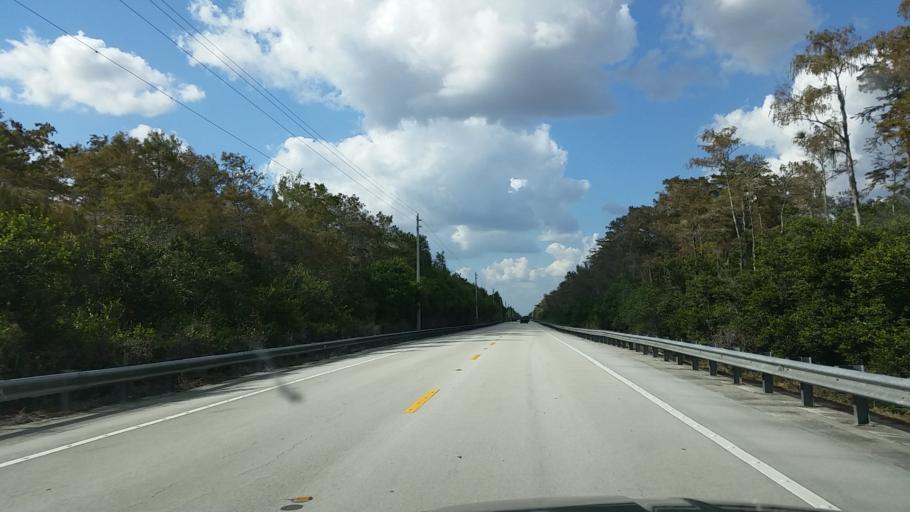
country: US
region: Florida
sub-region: Miami-Dade County
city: Kendall West
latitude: 25.7781
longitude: -80.8451
